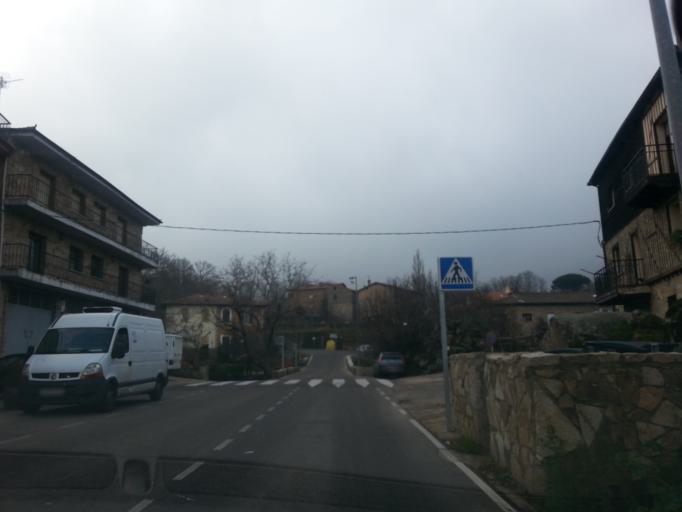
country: ES
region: Castille and Leon
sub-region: Provincia de Salamanca
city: La Alberca
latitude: 40.4890
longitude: -6.1077
